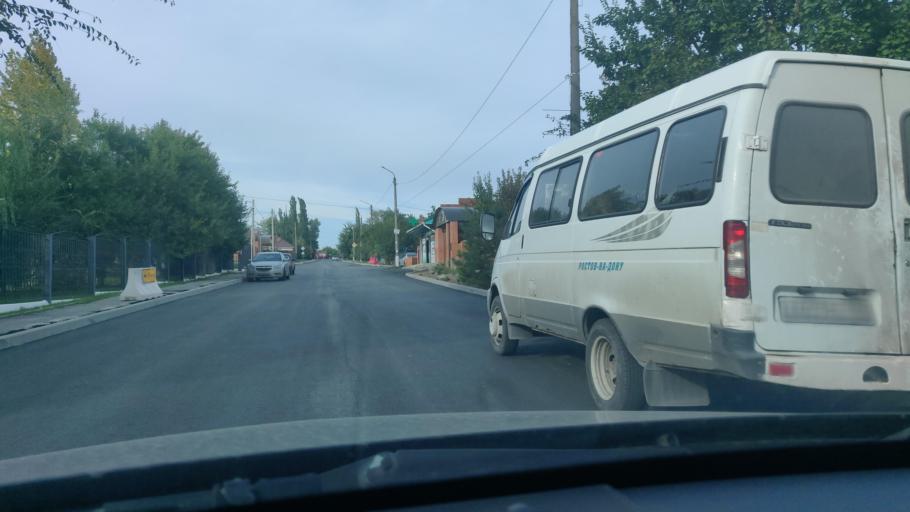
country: RU
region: Rostov
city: Ust'-Donetskiy
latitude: 47.6439
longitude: 40.8731
